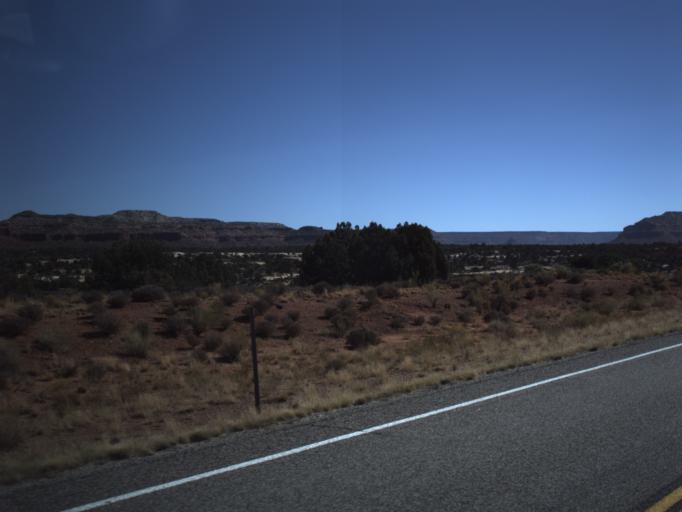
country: US
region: Utah
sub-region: San Juan County
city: Blanding
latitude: 37.6722
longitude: -110.2036
